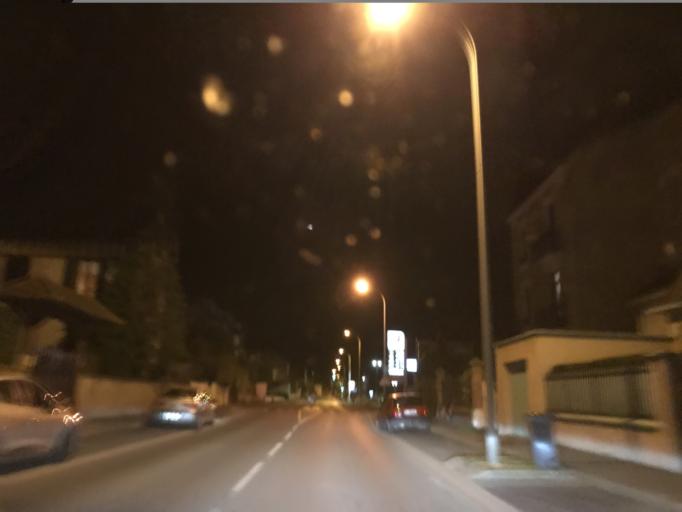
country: FR
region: Auvergne
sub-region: Departement de l'Allier
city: Vichy
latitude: 46.1168
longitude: 3.4373
